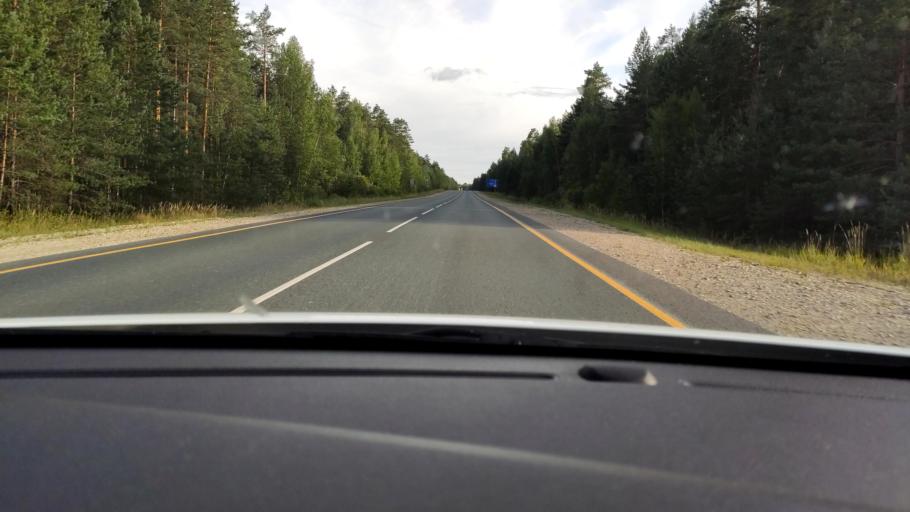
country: RU
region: Mariy-El
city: Suslonger
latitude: 56.2505
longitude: 48.2323
